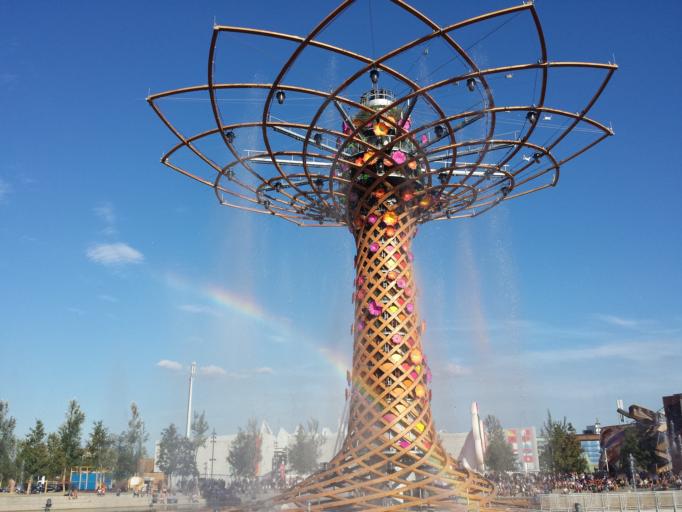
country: IT
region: Lombardy
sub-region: Citta metropolitana di Milano
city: Baranzate
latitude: 45.5209
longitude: 9.1066
